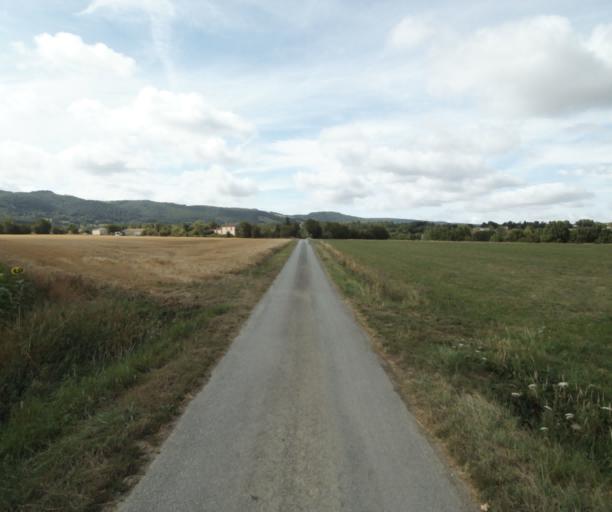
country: FR
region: Midi-Pyrenees
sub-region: Departement du Tarn
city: Soreze
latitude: 43.4756
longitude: 2.0852
